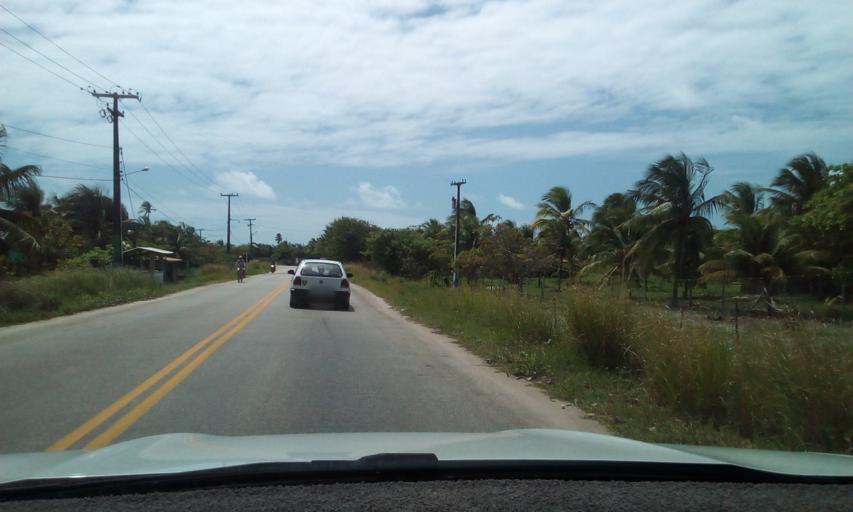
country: BR
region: Paraiba
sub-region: Rio Tinto
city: Rio Tinto
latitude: -6.7087
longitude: -34.9365
